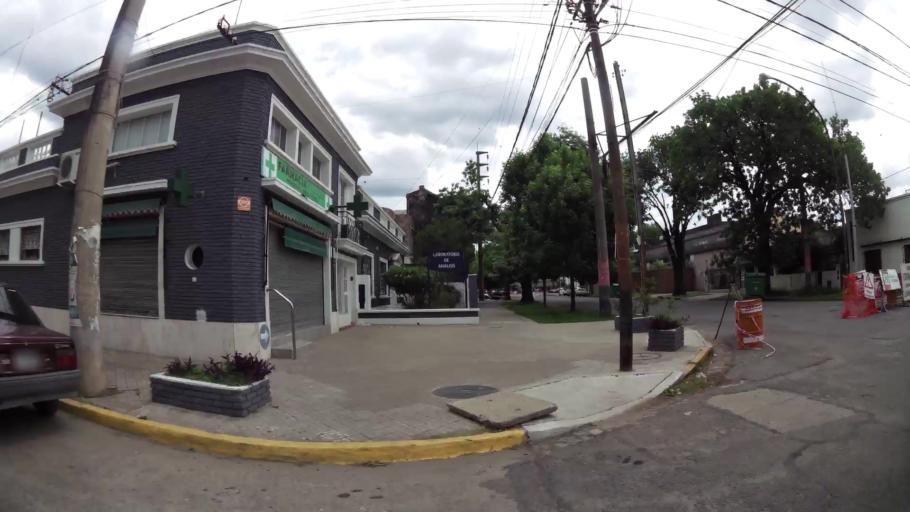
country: AR
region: Santa Fe
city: Gobernador Galvez
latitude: -32.9999
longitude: -60.6472
